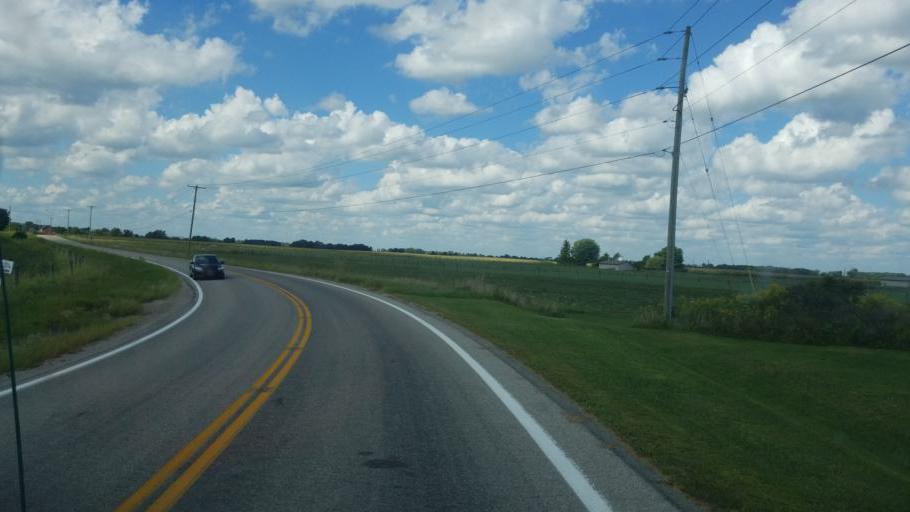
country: US
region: Ohio
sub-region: Union County
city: Richwood
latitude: 40.3602
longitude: -83.2606
